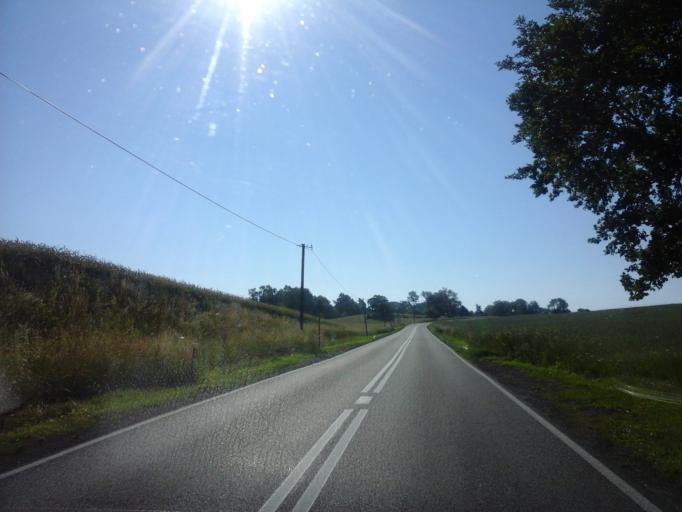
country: PL
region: West Pomeranian Voivodeship
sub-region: Powiat lobeski
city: Wegorzyno
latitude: 53.5062
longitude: 15.6523
